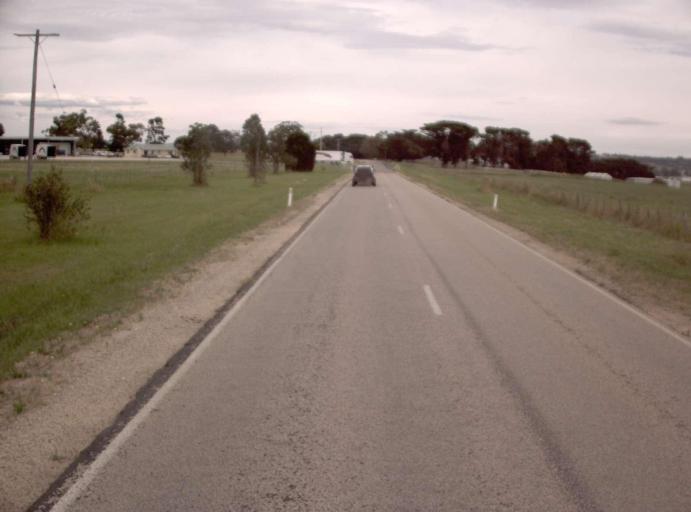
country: AU
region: Victoria
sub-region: East Gippsland
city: Bairnsdale
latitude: -37.8127
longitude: 147.4880
